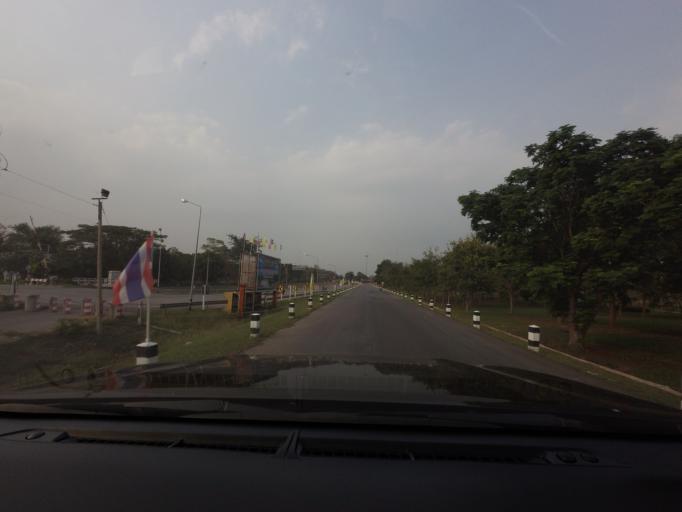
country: TH
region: Sara Buri
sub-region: Amphoe Wang Muang
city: Wang Muang
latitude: 14.8630
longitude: 101.0627
